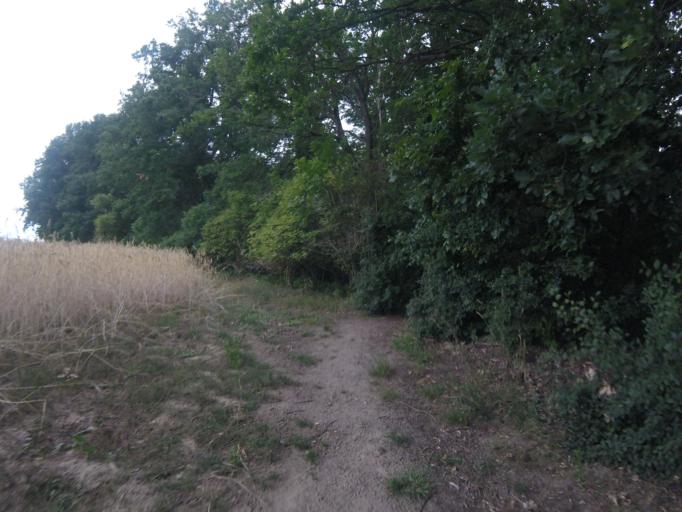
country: DE
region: Brandenburg
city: Bestensee
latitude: 52.2590
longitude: 13.6113
